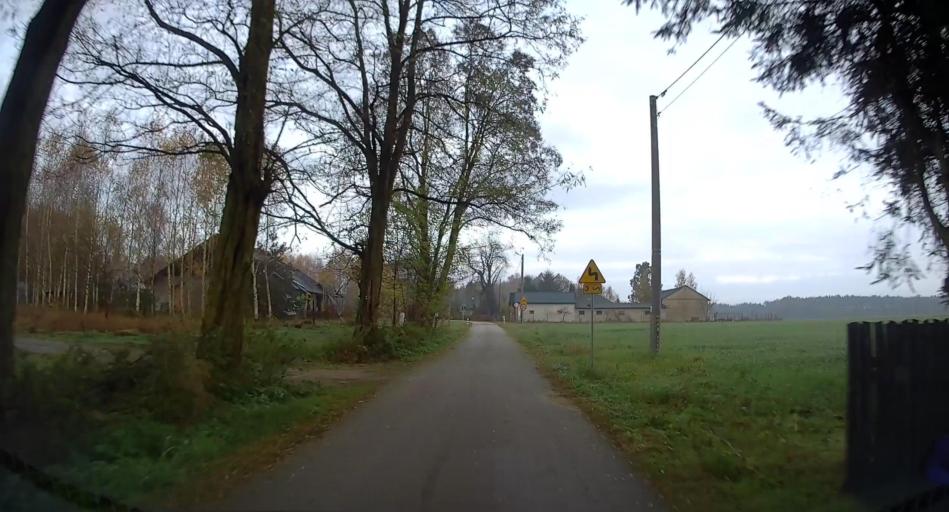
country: PL
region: Lodz Voivodeship
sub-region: Powiat skierniewicki
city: Kowiesy
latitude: 51.9365
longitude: 20.4012
